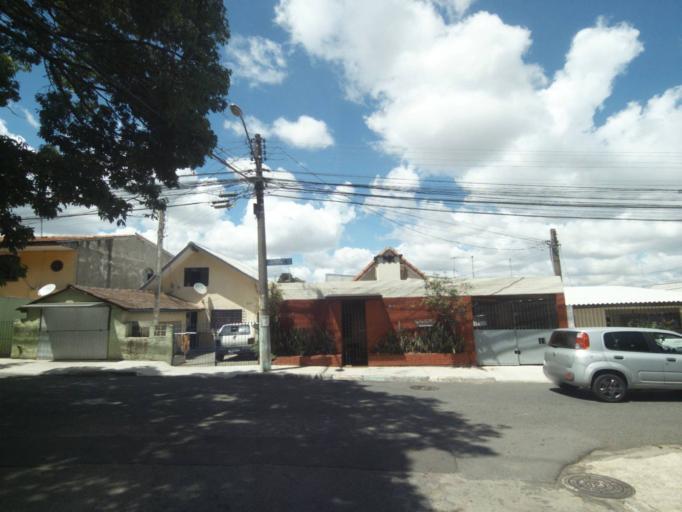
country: BR
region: Parana
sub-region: Curitiba
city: Curitiba
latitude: -25.5082
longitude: -49.3266
